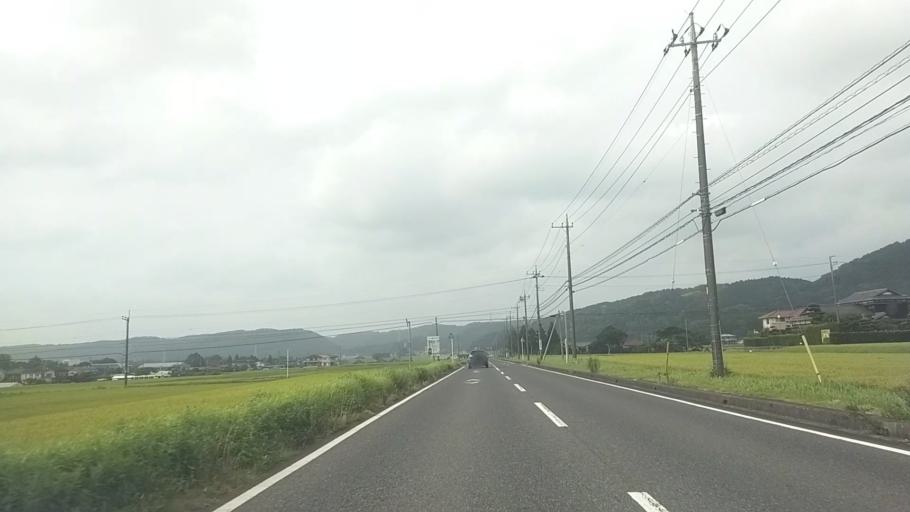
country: JP
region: Chiba
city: Kimitsu
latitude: 35.2857
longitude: 139.9902
